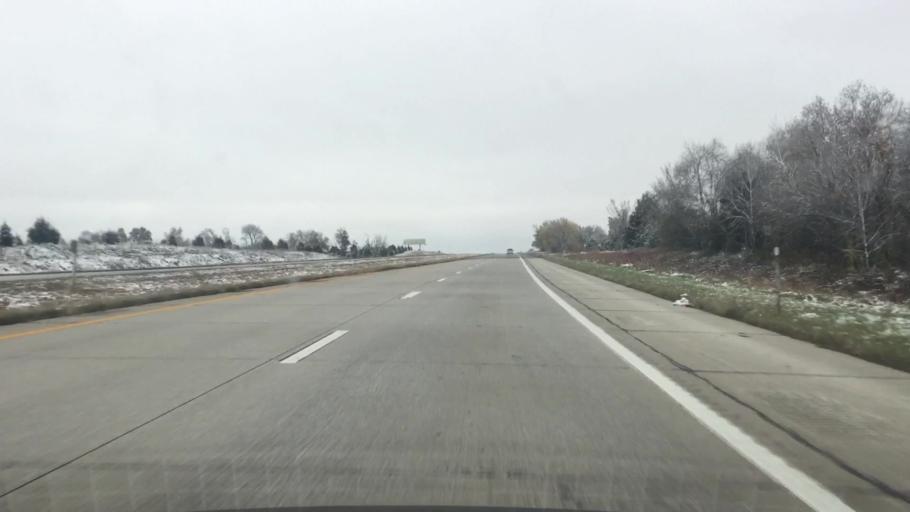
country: US
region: Missouri
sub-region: Saint Clair County
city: Osceola
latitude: 38.1737
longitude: -93.7220
